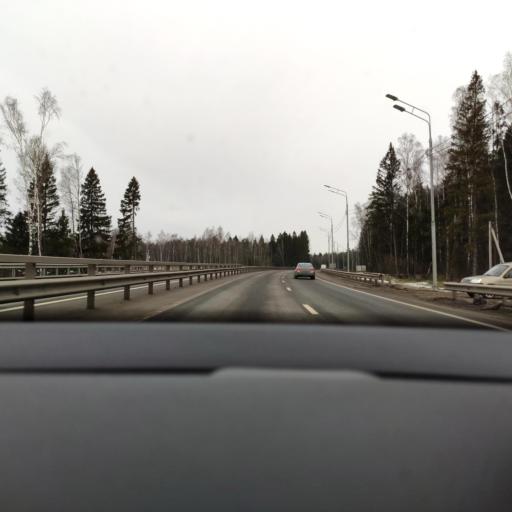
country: RU
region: Moskovskaya
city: Bol'shiye Vyazemy
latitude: 55.6483
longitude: 36.9876
